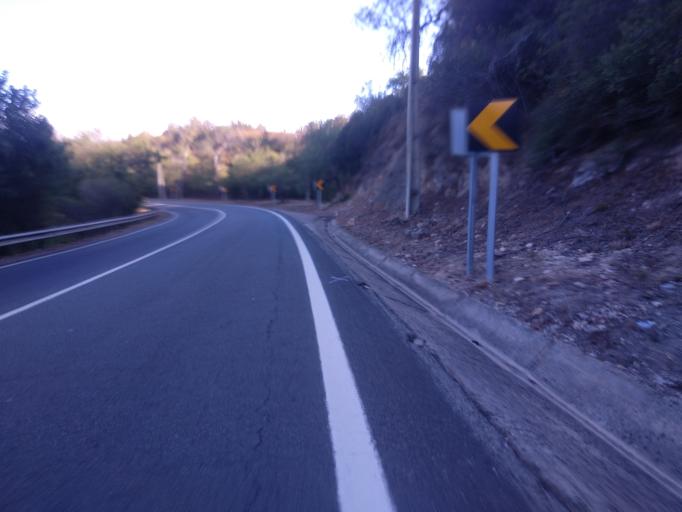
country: PT
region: Faro
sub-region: Sao Bras de Alportel
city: Sao Bras de Alportel
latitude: 37.1051
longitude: -7.9066
